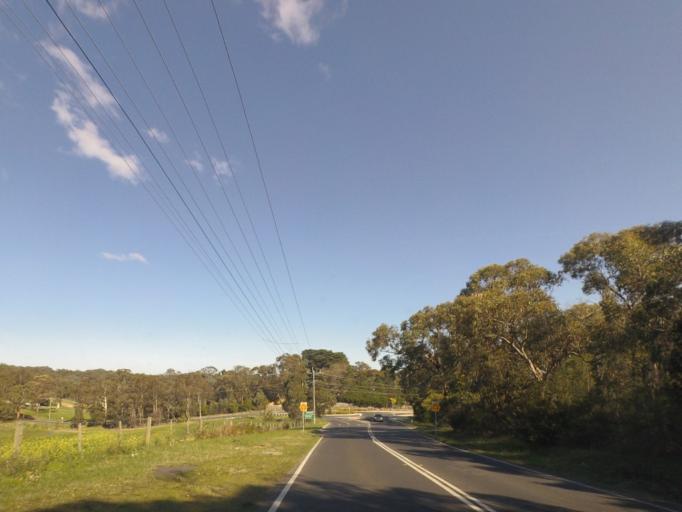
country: AU
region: Victoria
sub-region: Manningham
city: Park Orchards
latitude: -37.7705
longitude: 145.1999
